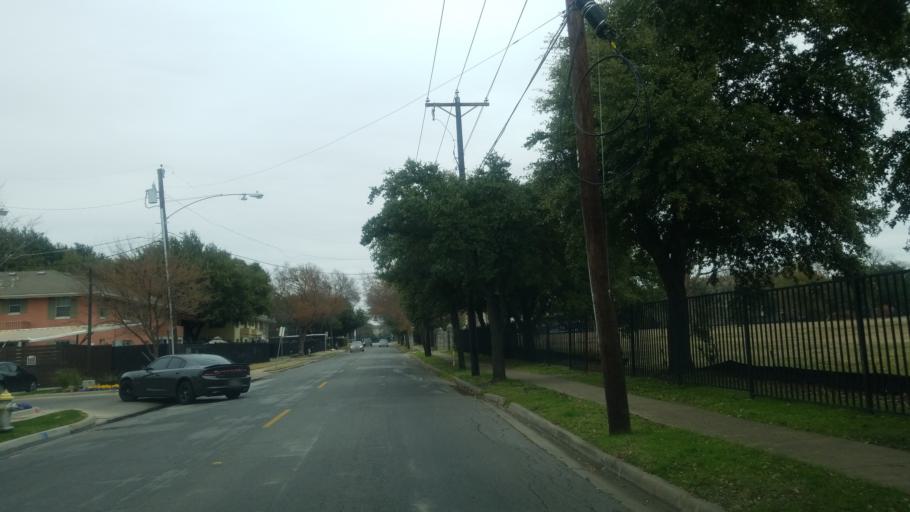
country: US
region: Texas
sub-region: Dallas County
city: Highland Park
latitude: 32.8157
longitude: -96.8229
